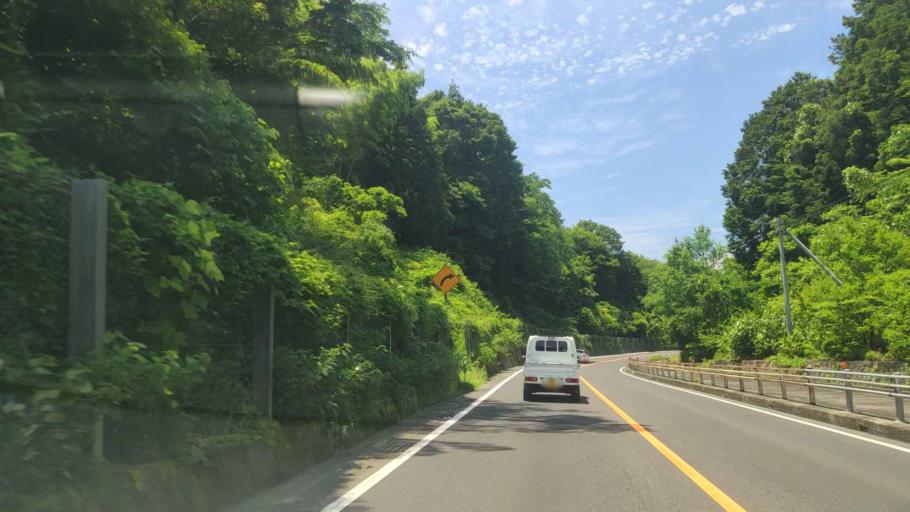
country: JP
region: Tottori
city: Tottori
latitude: 35.4010
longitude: 134.2620
